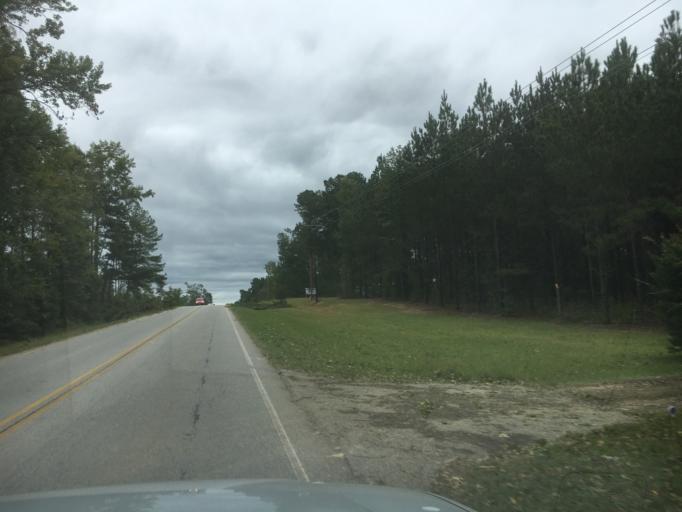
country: US
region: Georgia
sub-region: Lincoln County
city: Lincolnton
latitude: 33.7238
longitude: -82.5876
